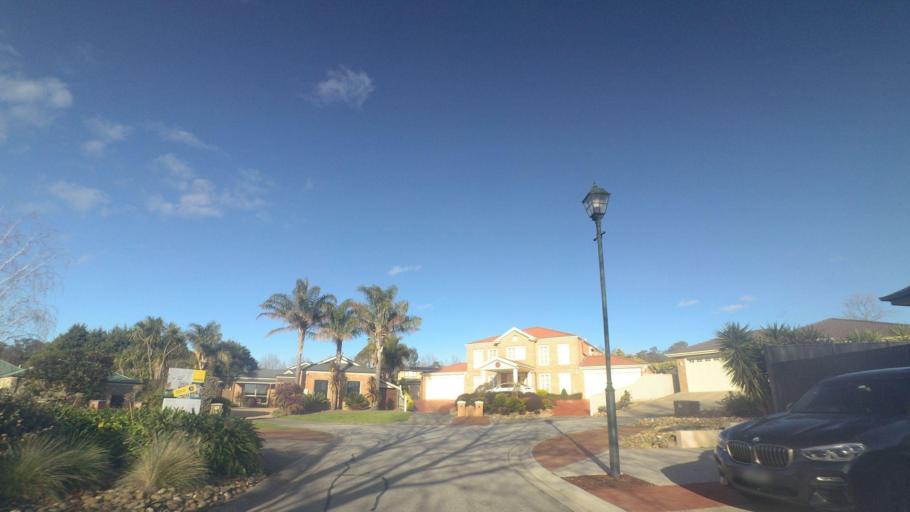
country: AU
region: Victoria
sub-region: Yarra Ranges
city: Lysterfield
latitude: -37.9195
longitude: 145.2869
